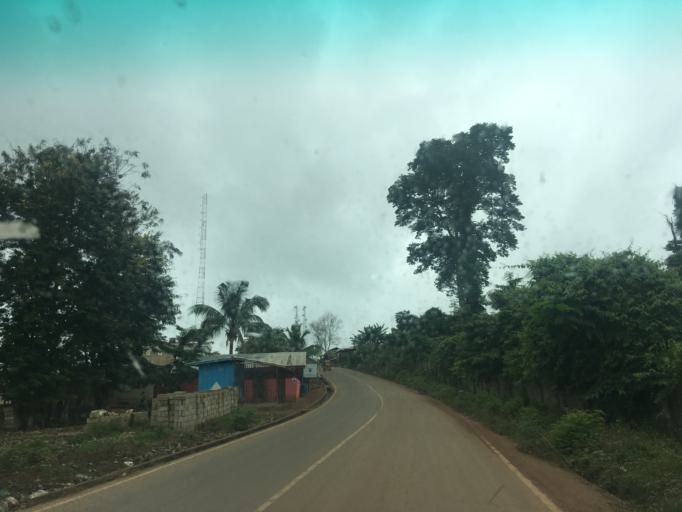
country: GH
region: Western
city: Wassa-Akropong
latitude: 5.8132
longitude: -2.4344
